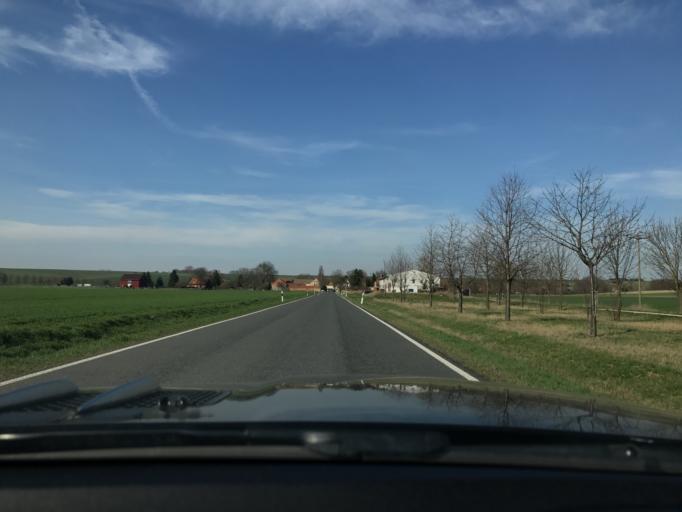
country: DE
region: Thuringia
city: Bothenheilingen
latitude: 51.1618
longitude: 10.6346
